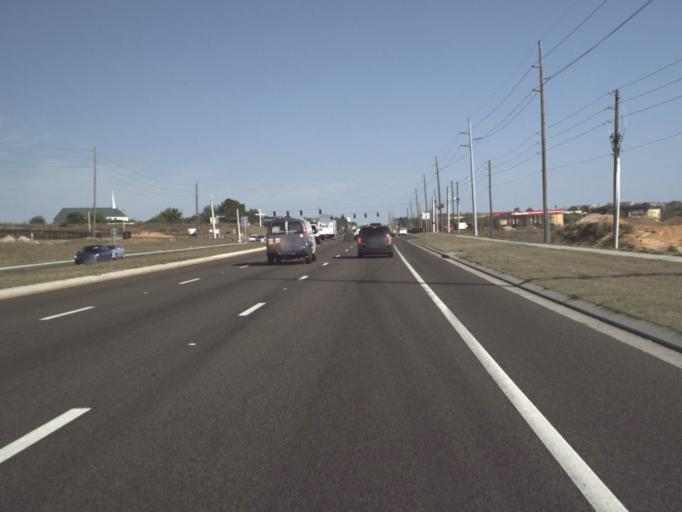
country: US
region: Florida
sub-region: Lake County
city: Clermont
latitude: 28.5174
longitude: -81.7269
